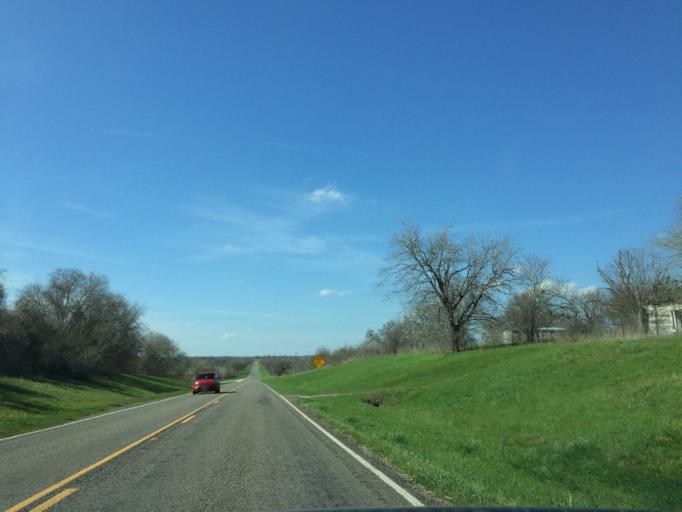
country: US
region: Texas
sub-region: Milam County
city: Thorndale
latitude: 30.5836
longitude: -97.1875
